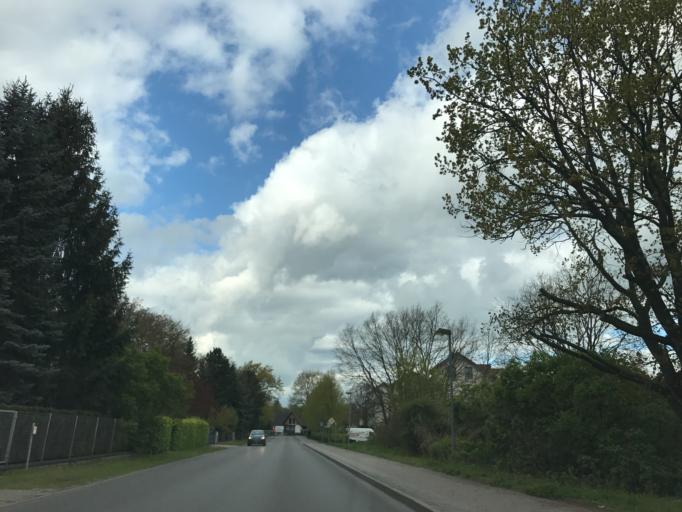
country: DE
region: Brandenburg
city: Brieselang
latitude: 52.5833
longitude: 12.9920
